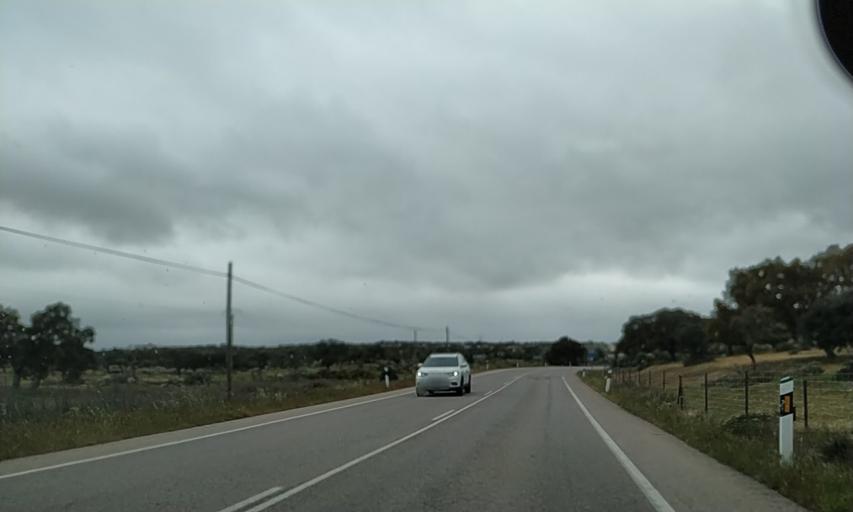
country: ES
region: Extremadura
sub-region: Provincia de Caceres
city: Malpartida de Caceres
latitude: 39.3917
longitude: -6.4298
